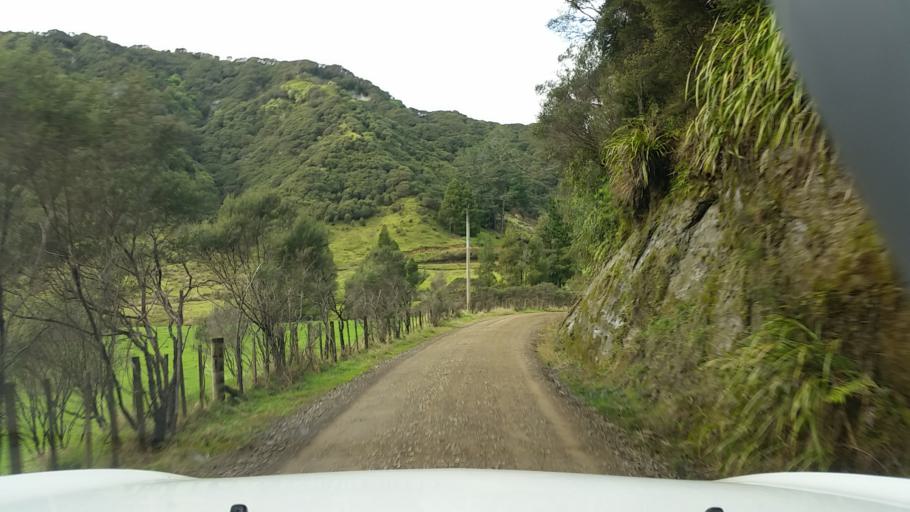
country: NZ
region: Taranaki
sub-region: New Plymouth District
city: Waitara
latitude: -38.8895
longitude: 174.7330
